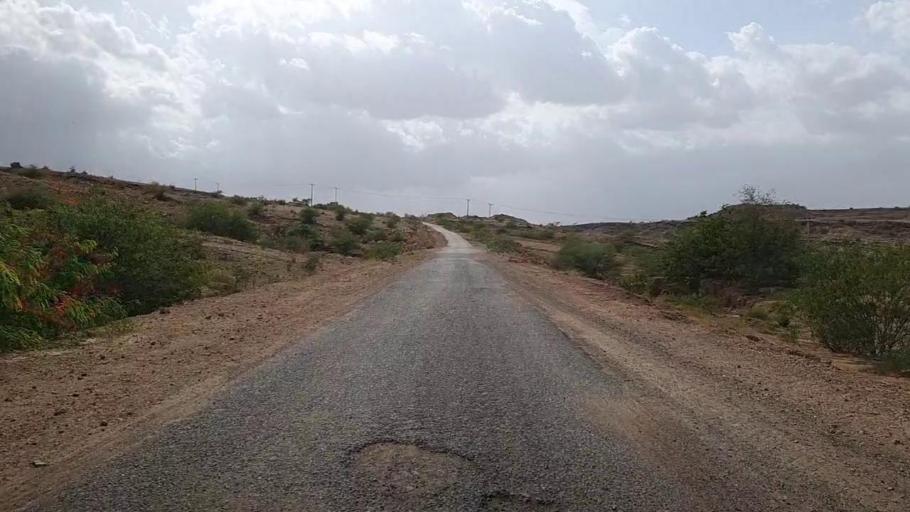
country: PK
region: Sindh
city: Jamshoro
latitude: 25.3962
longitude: 67.7417
